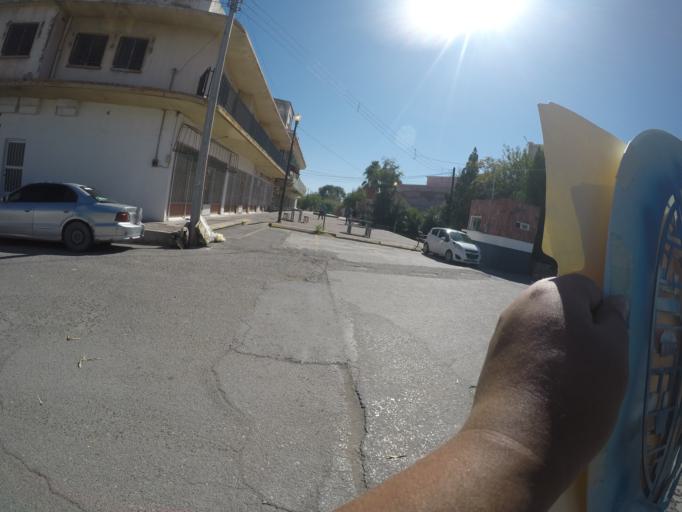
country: MX
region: Chihuahua
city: Ciudad Juarez
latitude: 31.7400
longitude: -106.4788
